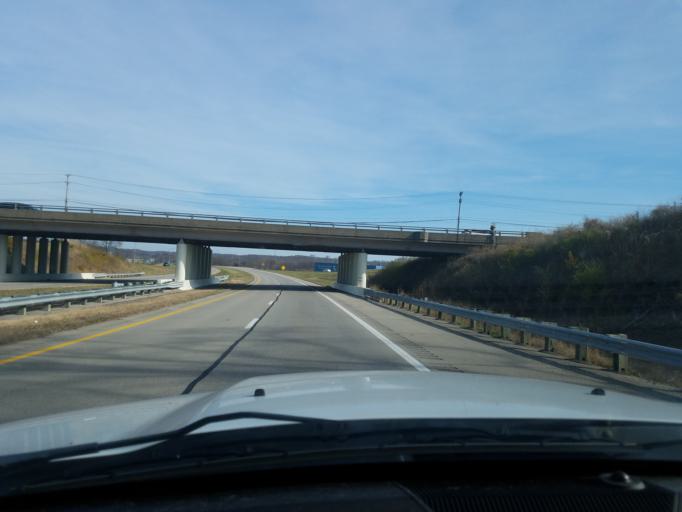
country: US
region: Ohio
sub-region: Jackson County
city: Jackson
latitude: 39.0383
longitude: -82.6283
